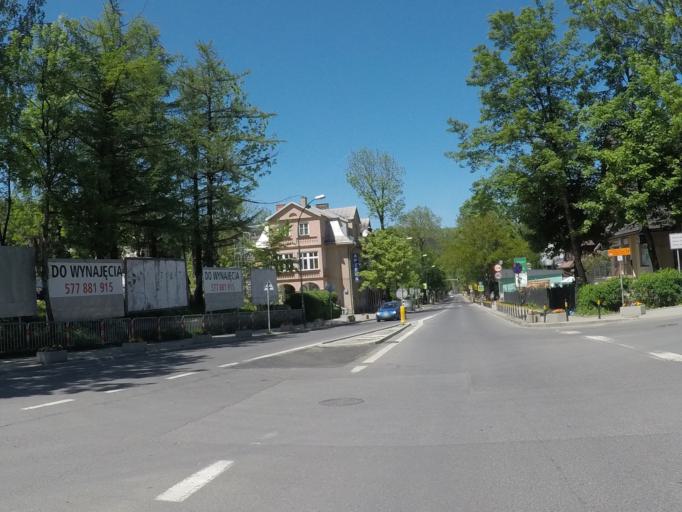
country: PL
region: Lesser Poland Voivodeship
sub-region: Powiat tatrzanski
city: Zakopane
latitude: 49.3003
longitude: 19.9616
